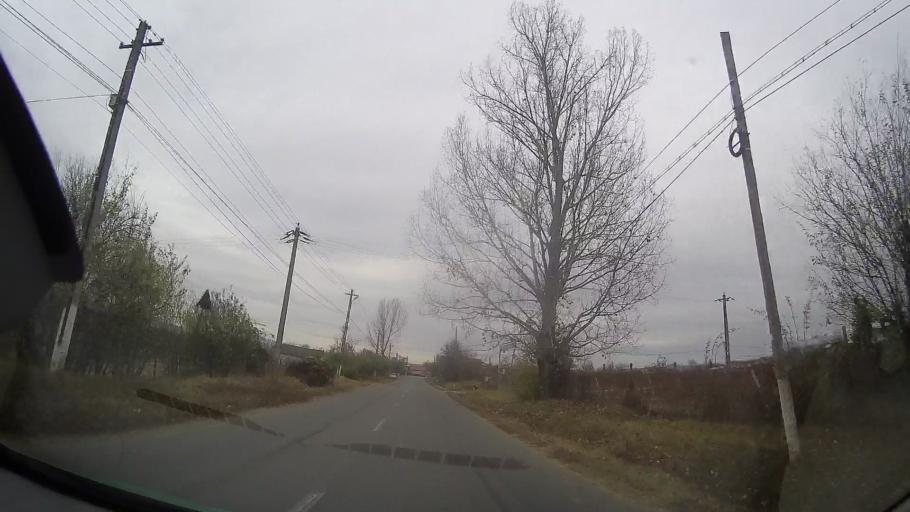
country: RO
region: Prahova
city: Mocesti
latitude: 45.0571
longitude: 26.2423
